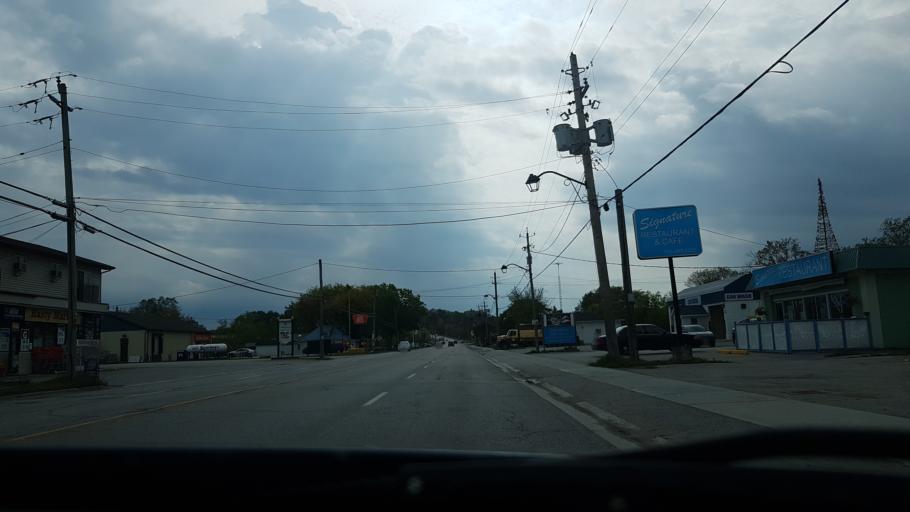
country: CA
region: Ontario
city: Omemee
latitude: 44.5311
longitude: -78.7401
